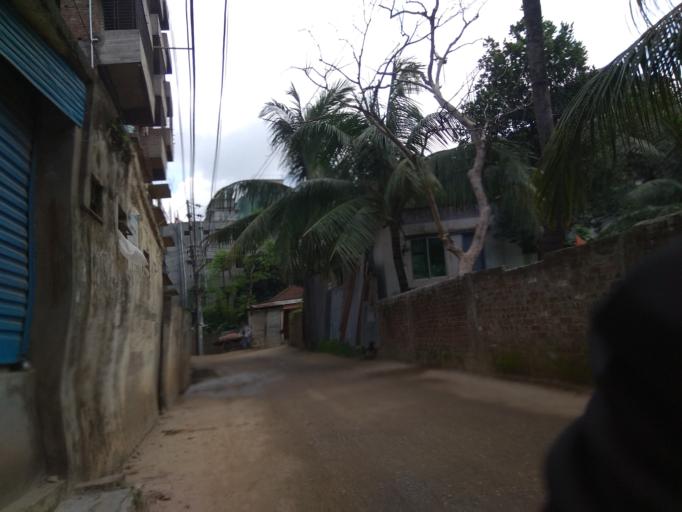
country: BD
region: Dhaka
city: Tungi
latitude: 23.8227
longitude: 90.3861
